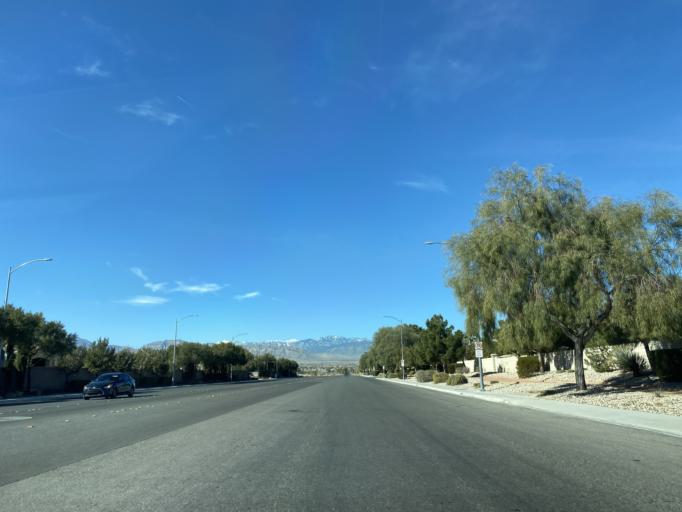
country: US
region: Nevada
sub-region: Clark County
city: North Las Vegas
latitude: 36.3051
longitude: -115.2358
